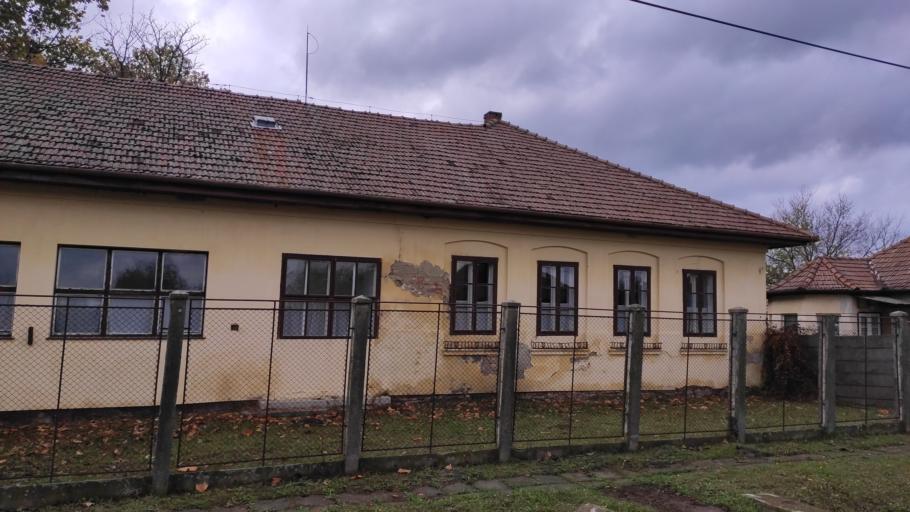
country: HU
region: Bekes
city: Mezobereny
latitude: 46.7627
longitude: 21.0406
